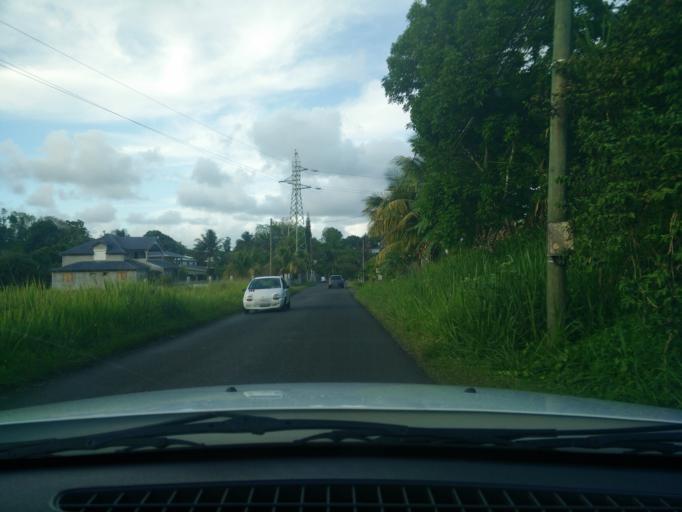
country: GP
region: Guadeloupe
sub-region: Guadeloupe
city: Les Abymes
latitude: 16.2533
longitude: -61.5064
